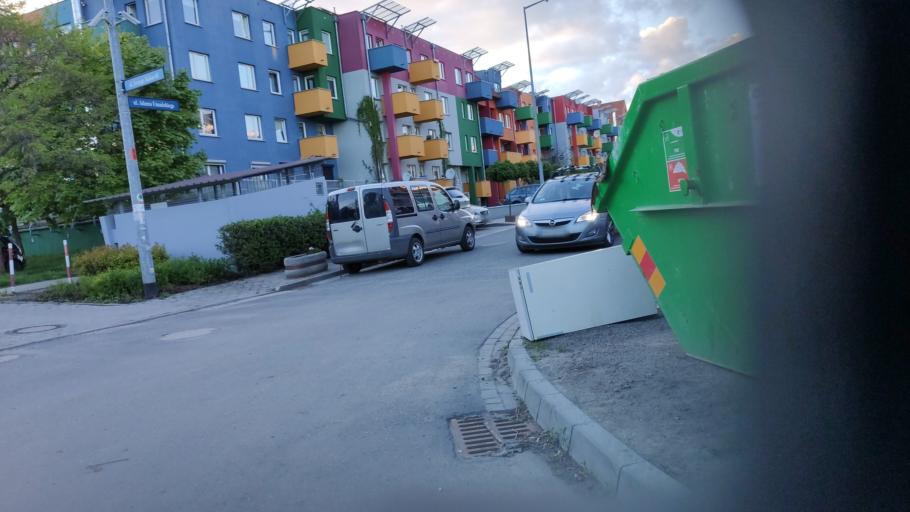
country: PL
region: Lower Silesian Voivodeship
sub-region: Powiat wroclawski
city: Wroclaw
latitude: 51.0717
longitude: 17.0389
